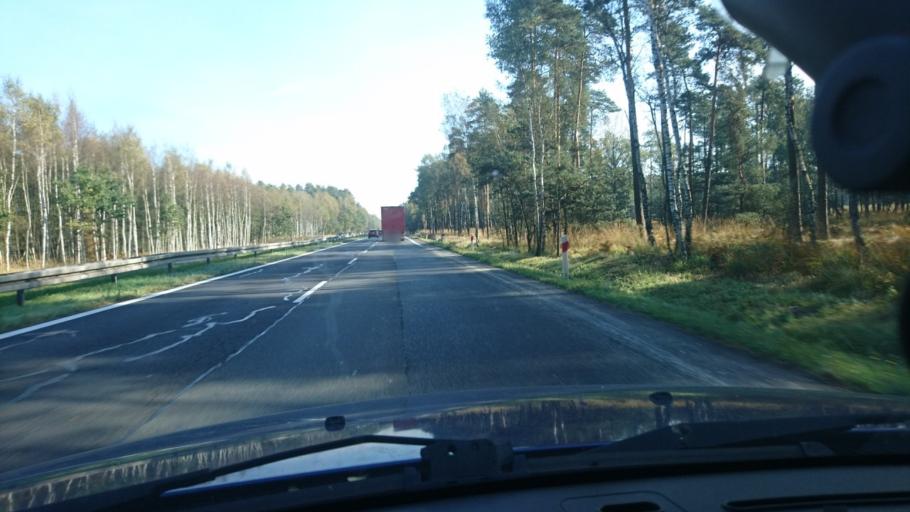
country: PL
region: Silesian Voivodeship
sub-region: Tychy
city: Cielmice
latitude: 50.0687
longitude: 18.9825
